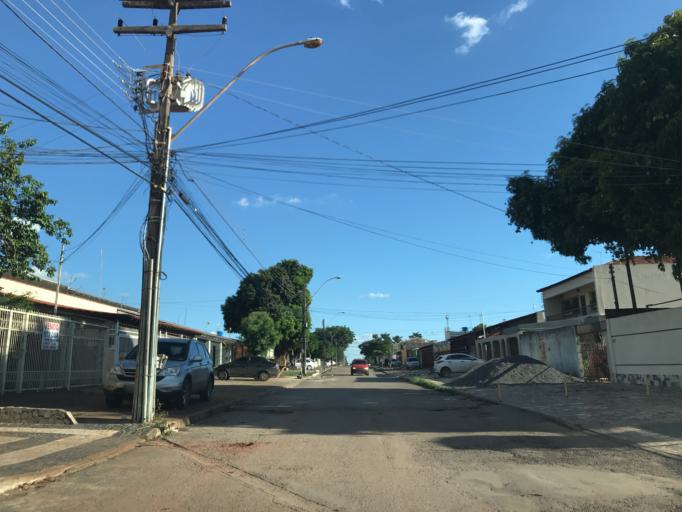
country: BR
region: Federal District
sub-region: Brasilia
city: Brasilia
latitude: -15.8031
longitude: -48.0666
